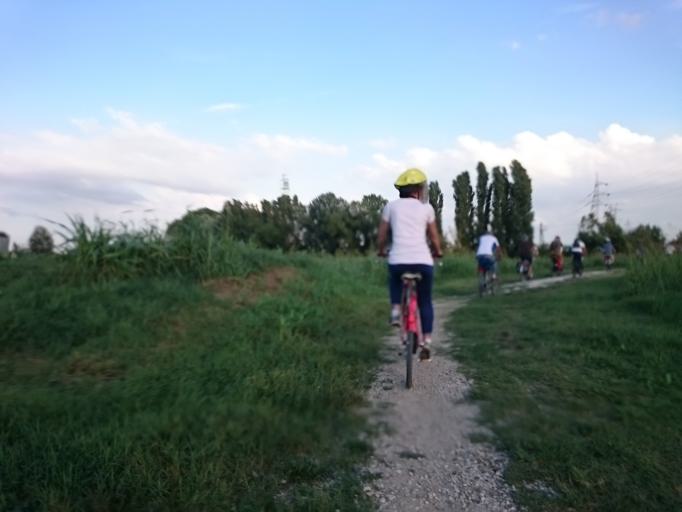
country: IT
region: Veneto
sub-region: Provincia di Padova
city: Noventa
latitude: 45.4064
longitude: 11.9221
